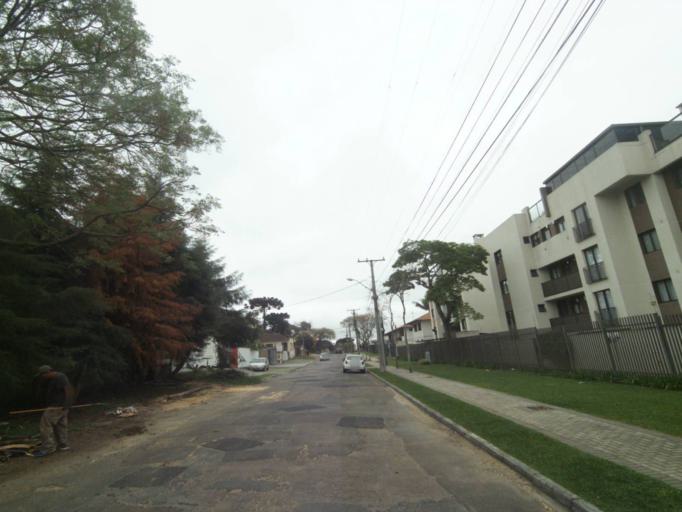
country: BR
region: Parana
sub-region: Curitiba
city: Curitiba
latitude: -25.4692
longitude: -49.2811
